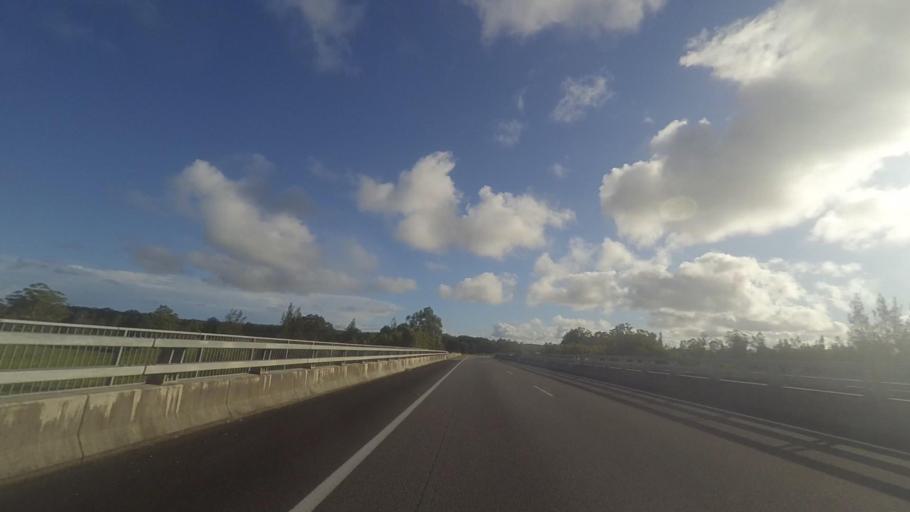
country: AU
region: New South Wales
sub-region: Great Lakes
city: Nabiac
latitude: -32.1056
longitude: 152.3741
